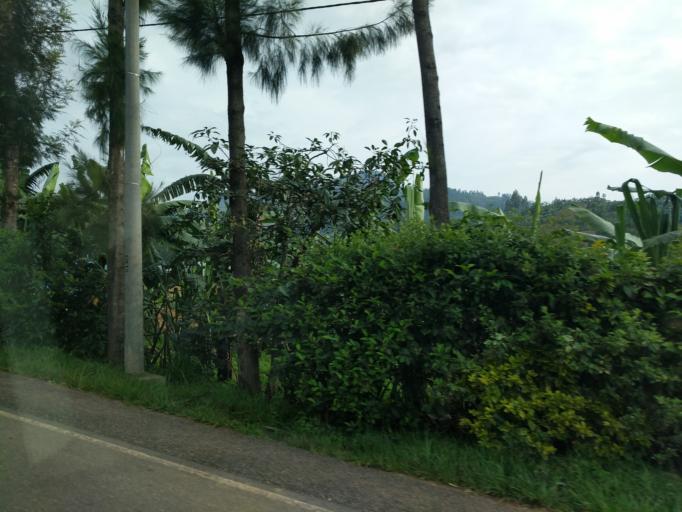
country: RW
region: Northern Province
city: Musanze
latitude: -1.6509
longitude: 29.8066
